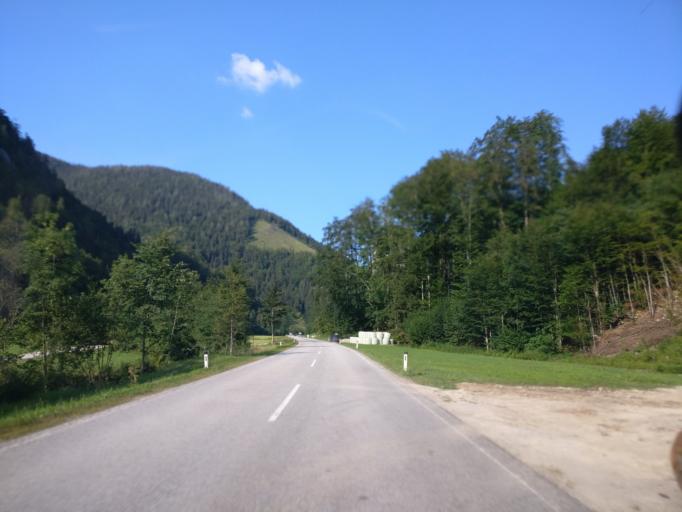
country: AT
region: Lower Austria
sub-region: Politischer Bezirk Scheibbs
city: Gostling an der Ybbs
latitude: 47.7368
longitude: 14.8786
